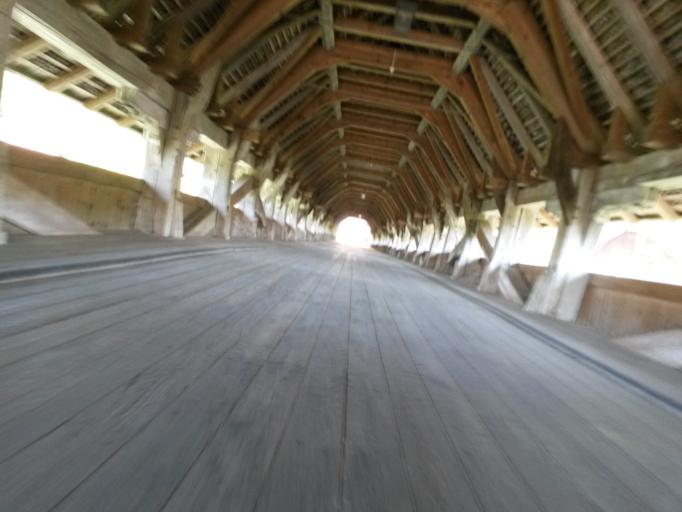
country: CH
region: Bern
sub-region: Bern-Mittelland District
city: Muhleberg
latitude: 46.9440
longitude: 7.2429
